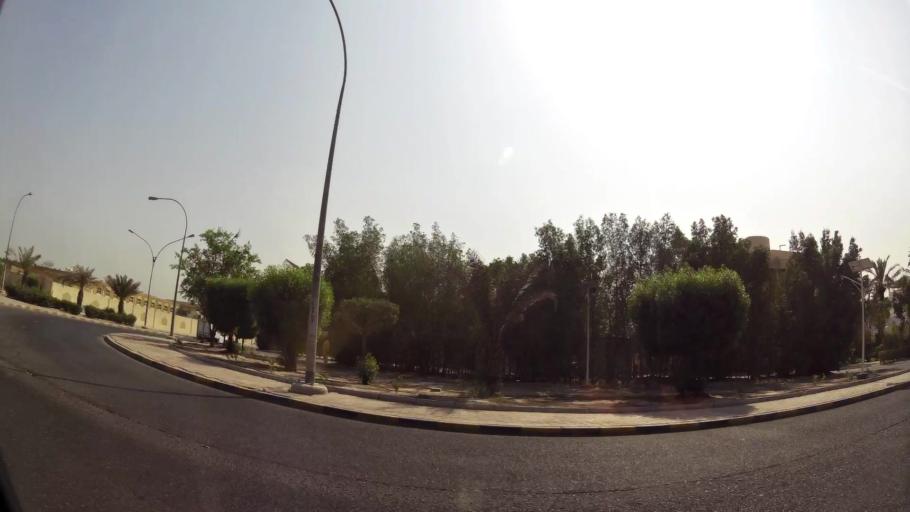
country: KW
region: Al Asimah
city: Ad Dasmah
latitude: 29.3473
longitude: 47.9880
